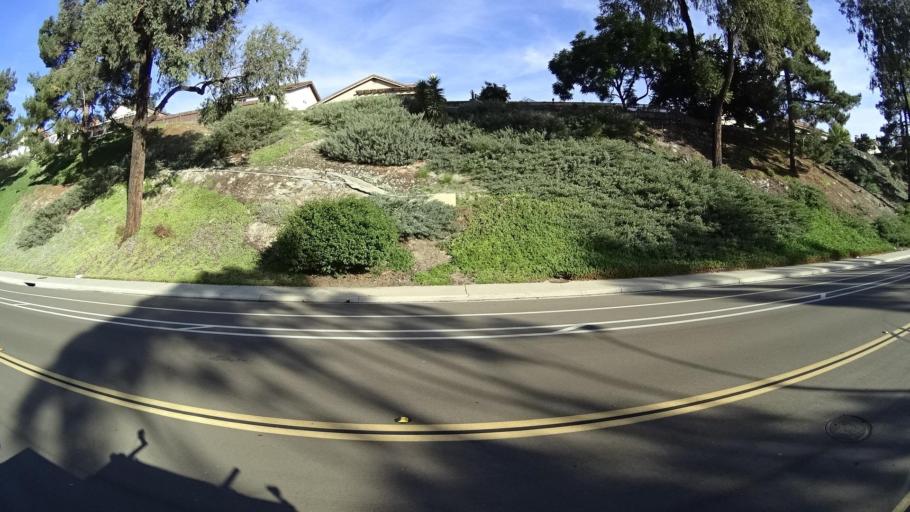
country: US
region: California
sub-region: San Diego County
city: Casa de Oro-Mount Helix
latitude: 32.7312
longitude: -116.9671
